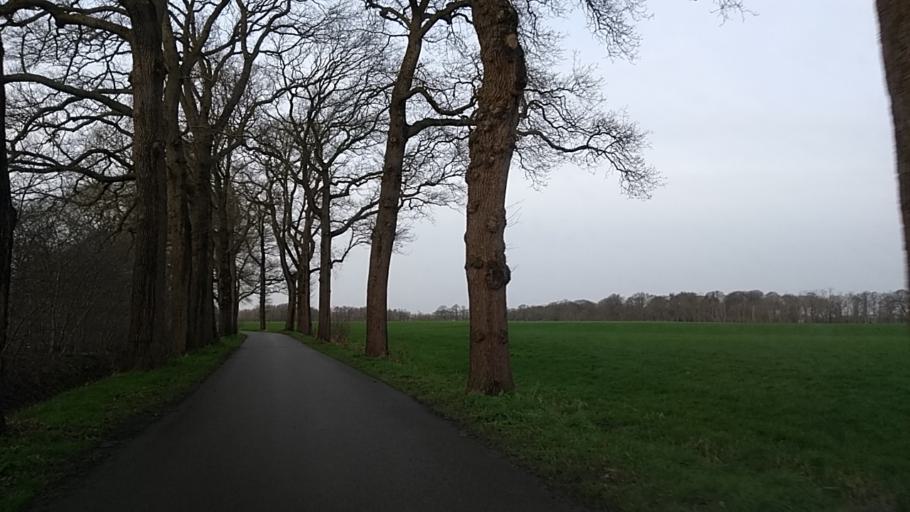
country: NL
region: Overijssel
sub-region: Gemeente Deventer
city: Schalkhaar
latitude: 52.2641
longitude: 6.2589
